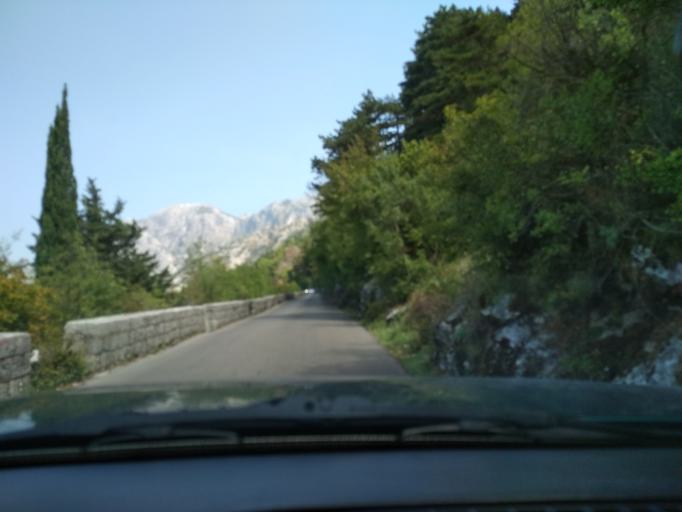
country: ME
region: Kotor
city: Kotor
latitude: 42.4033
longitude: 18.7751
